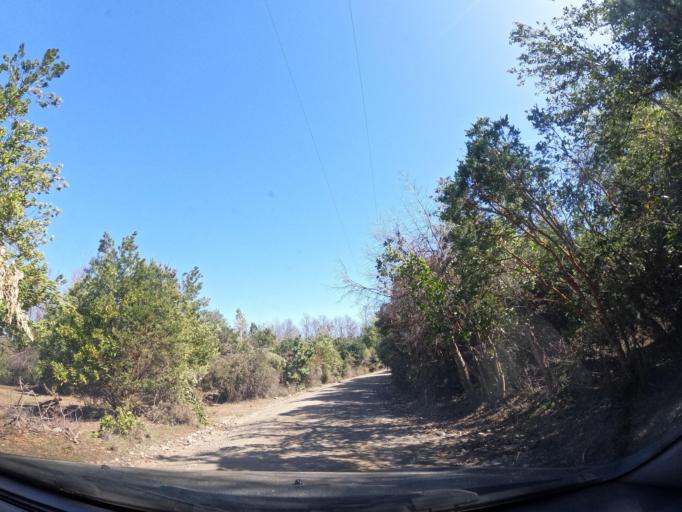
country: CL
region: Maule
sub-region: Provincia de Linares
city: Longavi
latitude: -36.2475
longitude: -71.3328
